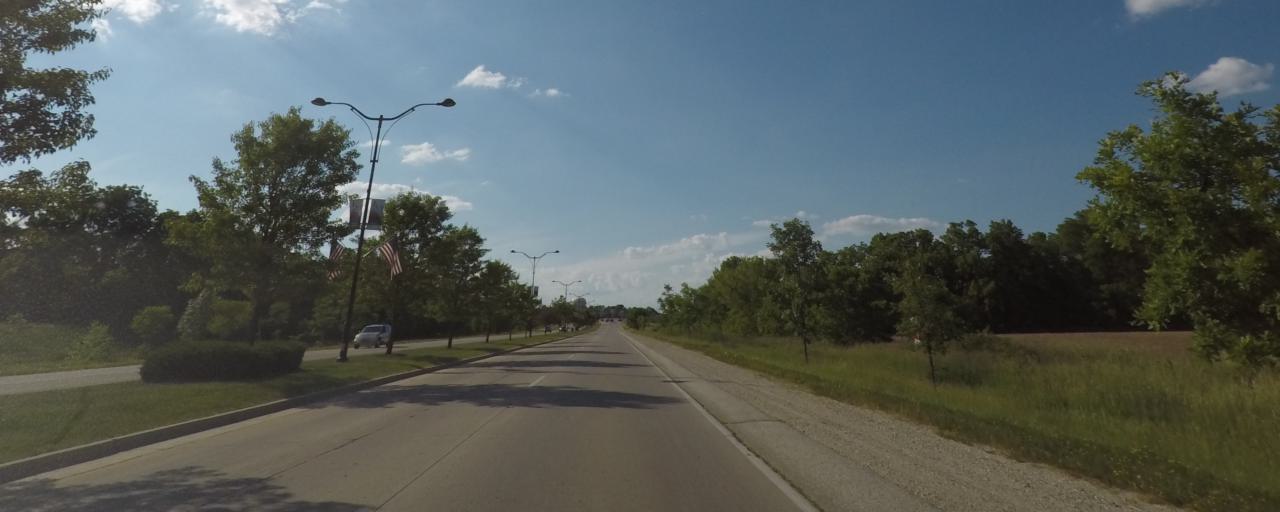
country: US
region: Wisconsin
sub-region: Waukesha County
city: Muskego
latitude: 42.9222
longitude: -88.1107
